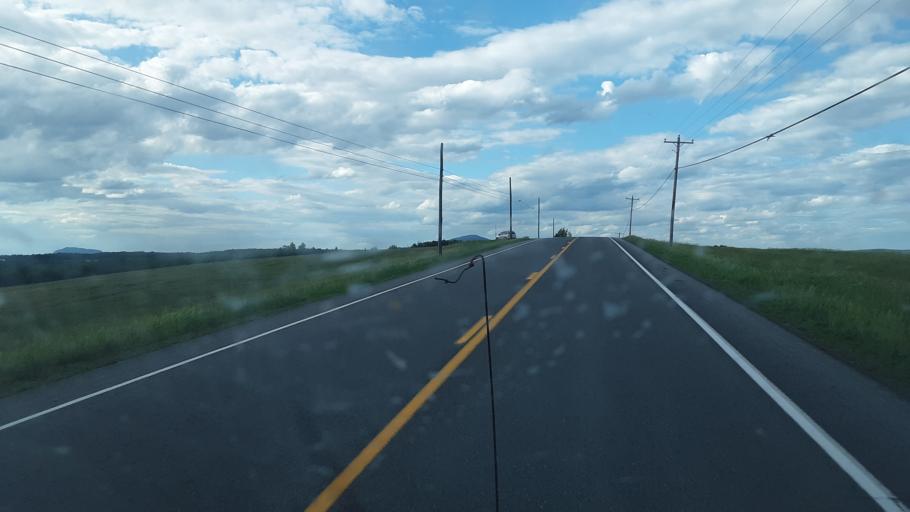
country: US
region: Maine
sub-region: Penobscot County
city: Patten
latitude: 45.9525
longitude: -68.4523
